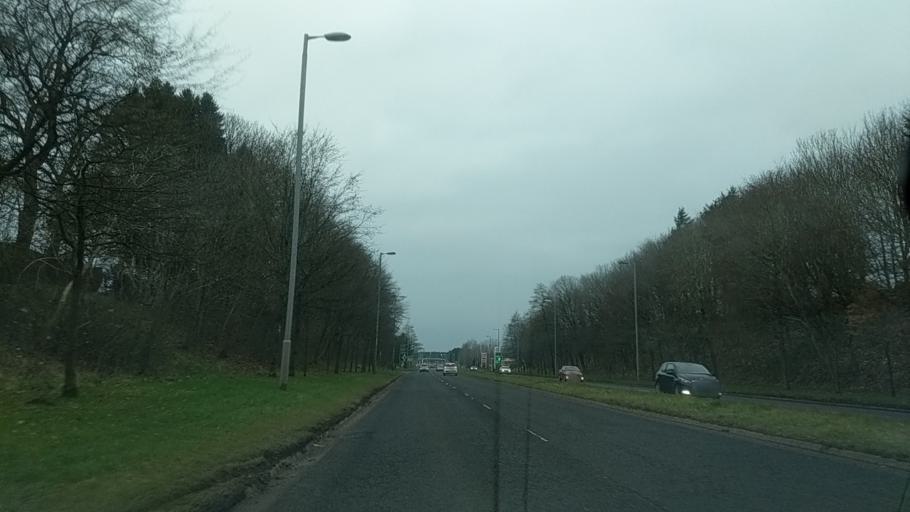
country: GB
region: Scotland
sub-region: South Lanarkshire
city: East Kilbride
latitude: 55.7632
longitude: -4.2012
